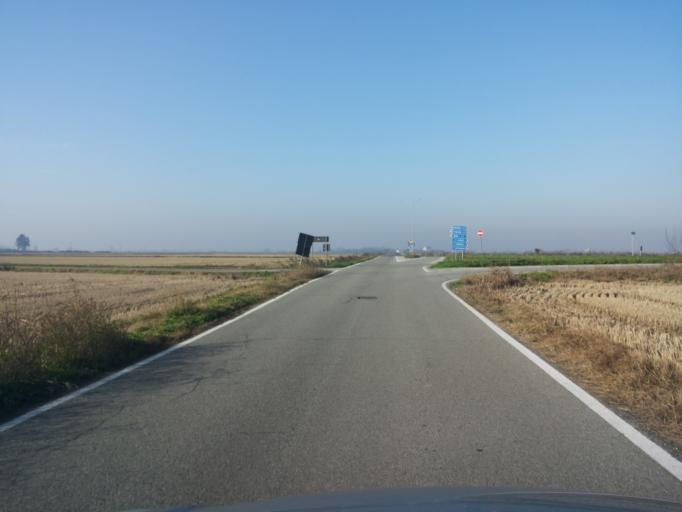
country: IT
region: Piedmont
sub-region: Provincia di Vercelli
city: Stroppiana
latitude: 45.2309
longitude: 8.4464
